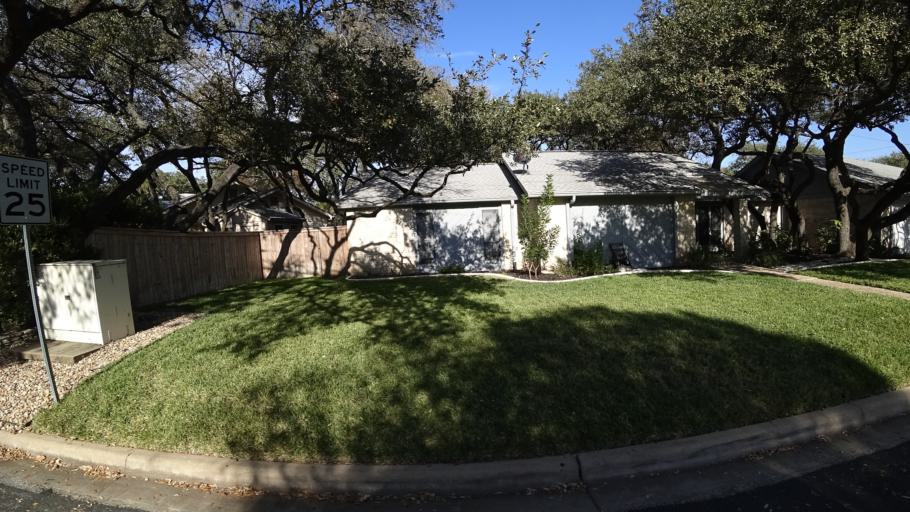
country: US
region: Texas
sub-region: Williamson County
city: Jollyville
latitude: 30.3767
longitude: -97.7545
